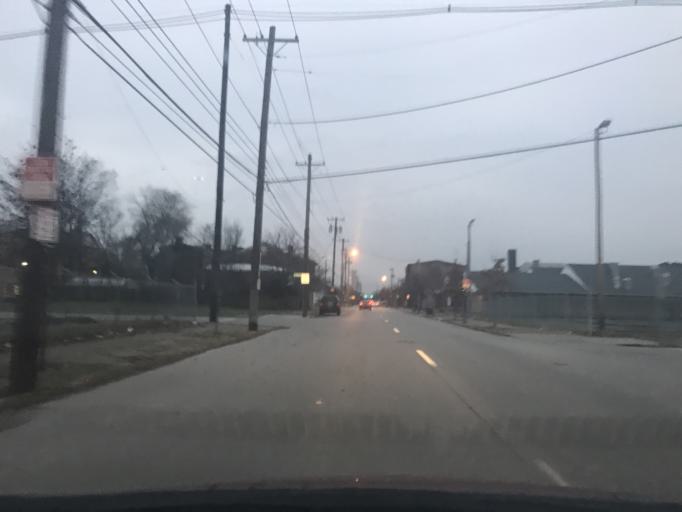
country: US
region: Kentucky
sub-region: Jefferson County
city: Louisville
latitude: 38.2439
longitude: -85.7478
